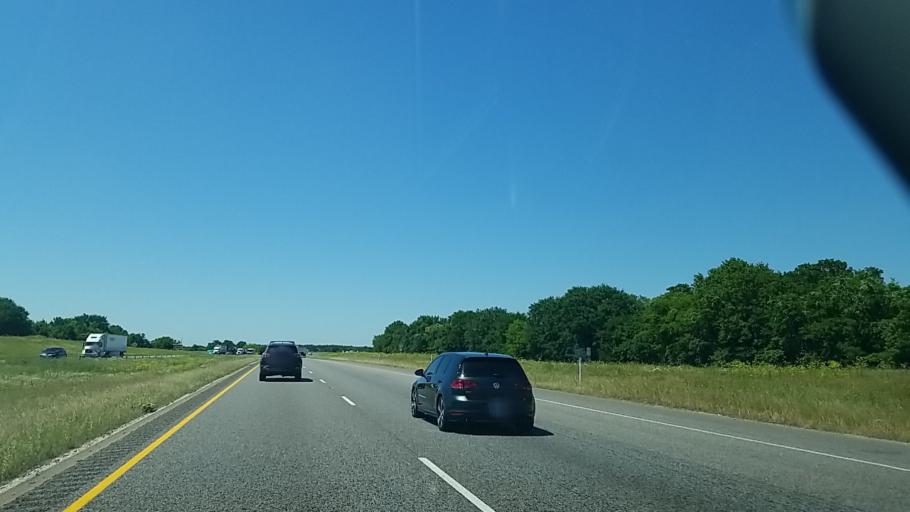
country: US
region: Texas
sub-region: Freestone County
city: Fairfield
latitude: 31.6002
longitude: -96.1549
